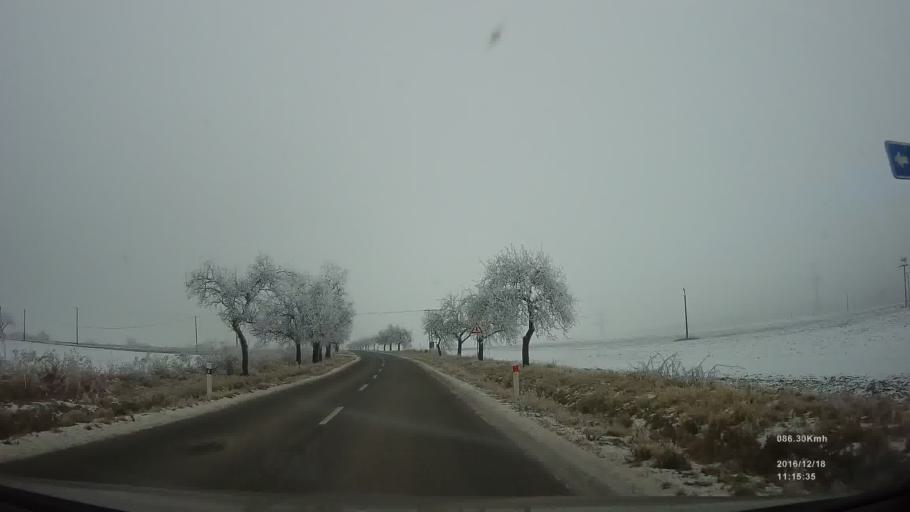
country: SK
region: Presovsky
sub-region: Okres Presov
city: Presov
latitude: 48.9069
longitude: 21.3244
